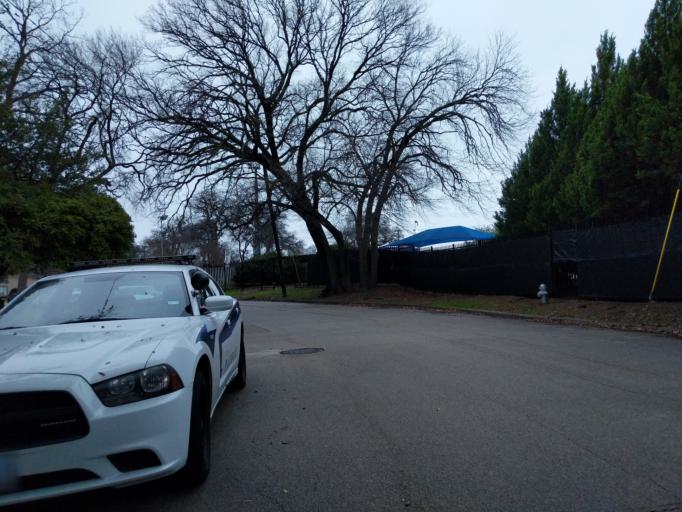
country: US
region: Texas
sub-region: Dallas County
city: University Park
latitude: 32.9006
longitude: -96.7716
